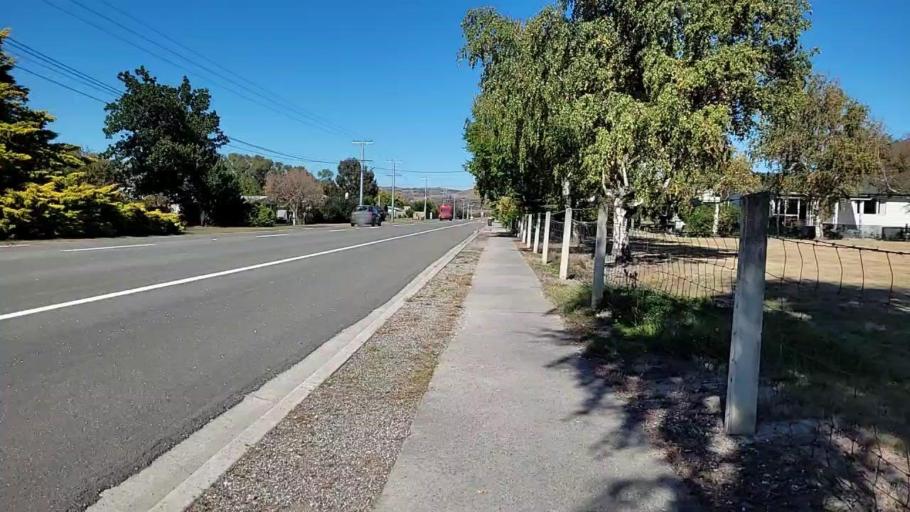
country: NZ
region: Otago
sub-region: Queenstown-Lakes District
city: Wanaka
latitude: -45.1007
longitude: 169.5966
